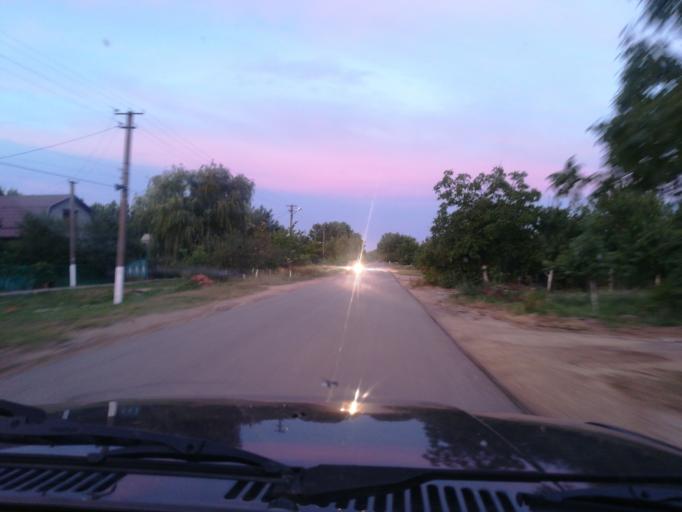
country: RU
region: Krasnodarskiy
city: Yurovka
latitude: 45.1143
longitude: 37.4267
